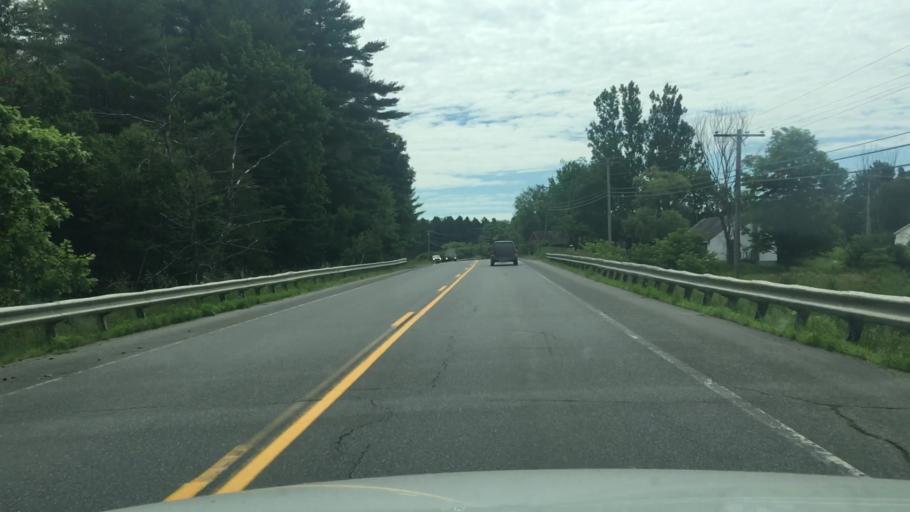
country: US
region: Maine
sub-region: Waldo County
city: Troy
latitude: 44.6115
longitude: -69.3134
